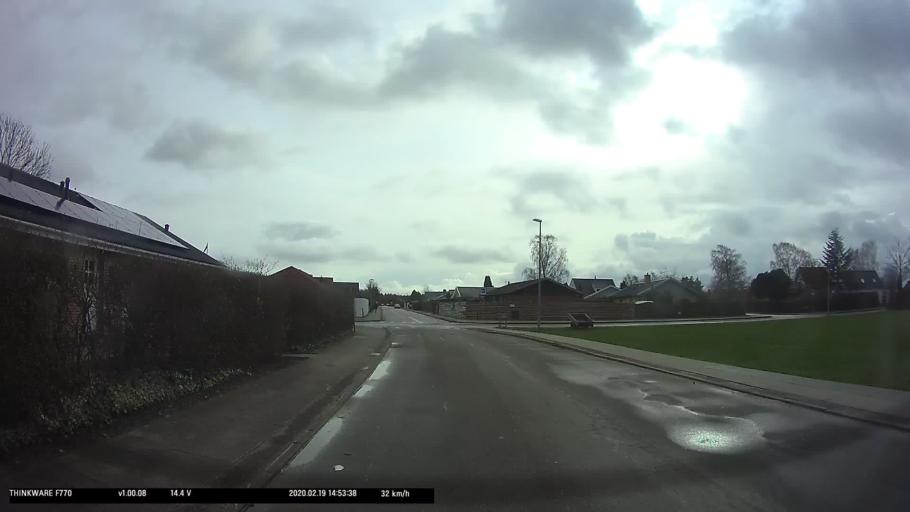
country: DK
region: Capital Region
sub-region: Tarnby Kommune
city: Tarnby
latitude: 55.5900
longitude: 12.5721
